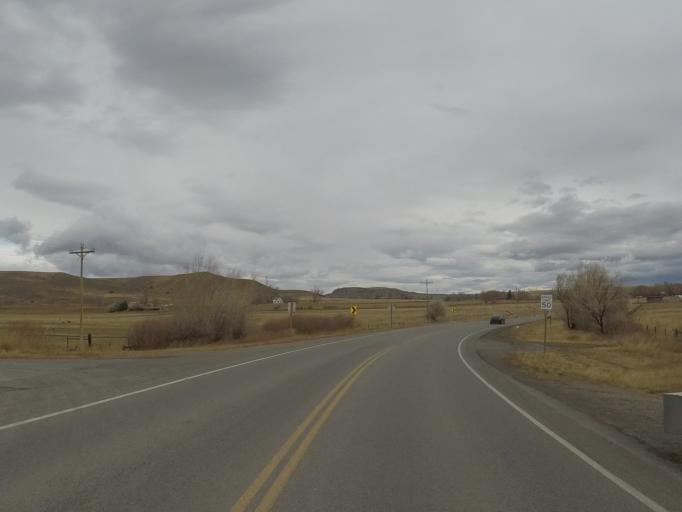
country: US
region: Montana
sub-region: Sweet Grass County
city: Big Timber
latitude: 45.8481
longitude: -109.9408
